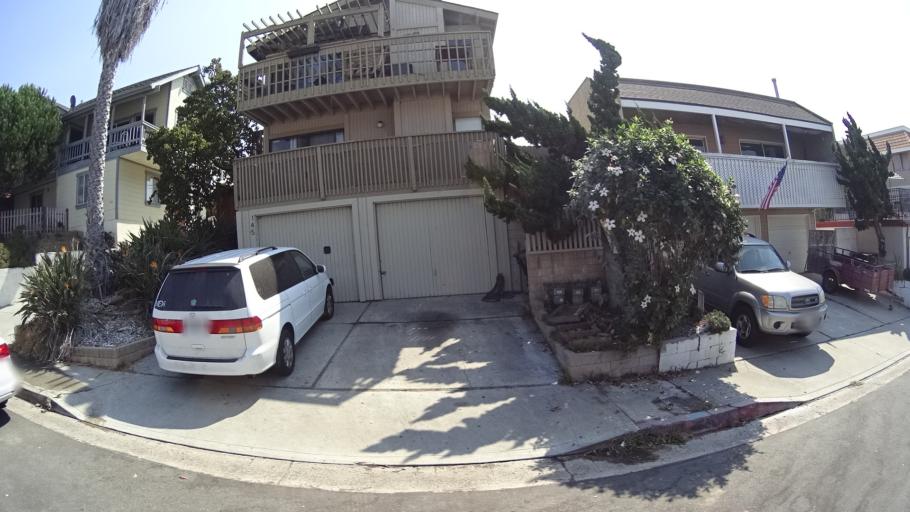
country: US
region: California
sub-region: Orange County
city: San Clemente
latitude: 33.4279
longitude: -117.6207
